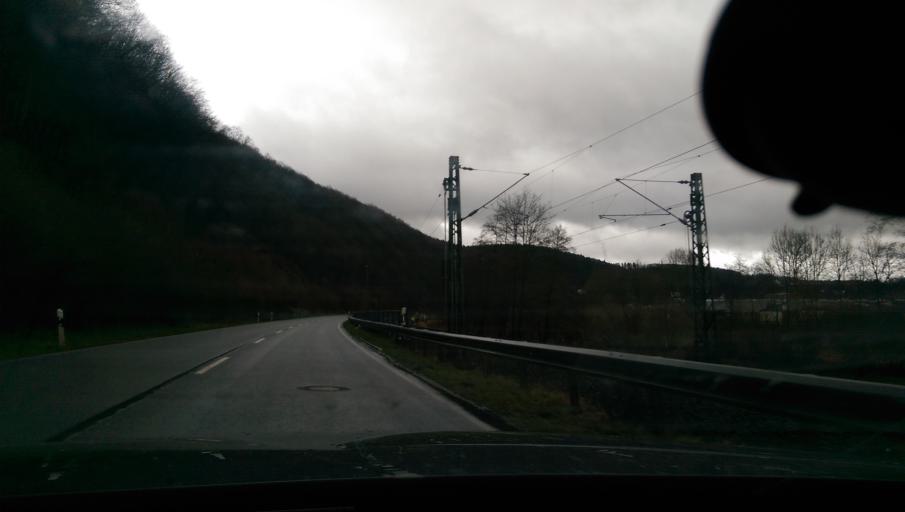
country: DE
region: North Rhine-Westphalia
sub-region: Regierungsbezirk Arnsberg
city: Finnentrop
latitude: 51.1929
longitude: 7.9687
